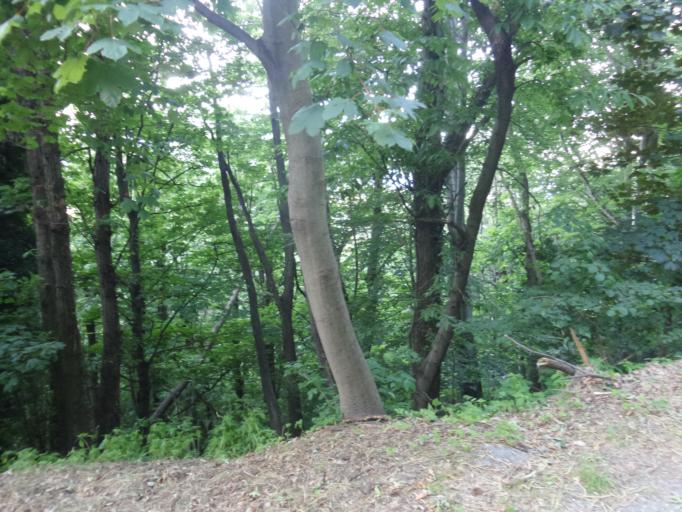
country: CH
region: Ticino
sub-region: Lugano District
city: Tesserete
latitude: 46.0804
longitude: 8.9958
